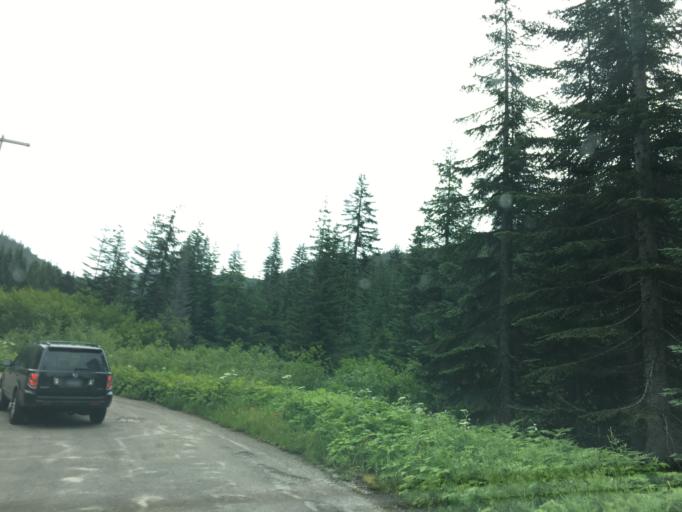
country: US
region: Washington
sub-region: Chelan County
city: Leavenworth
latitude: 47.7492
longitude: -121.1144
